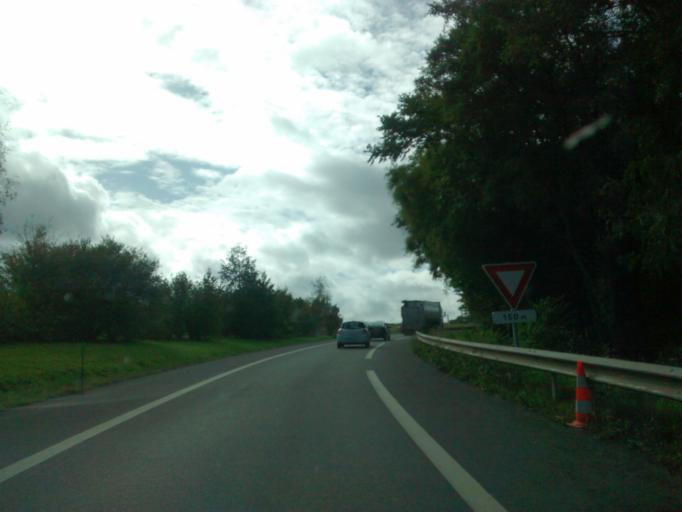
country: FR
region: Brittany
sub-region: Departement d'Ille-et-Vilaine
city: Chateaubourg
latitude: 48.1010
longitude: -1.4196
